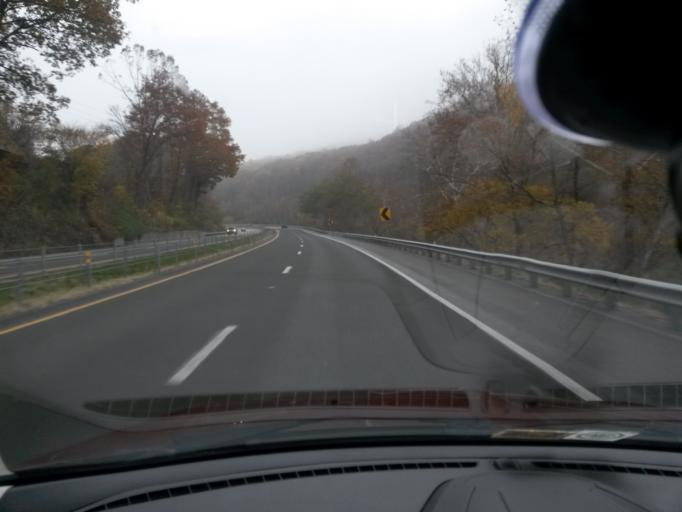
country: US
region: Virginia
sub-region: City of Covington
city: Fairlawn
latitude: 37.7802
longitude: -79.9292
